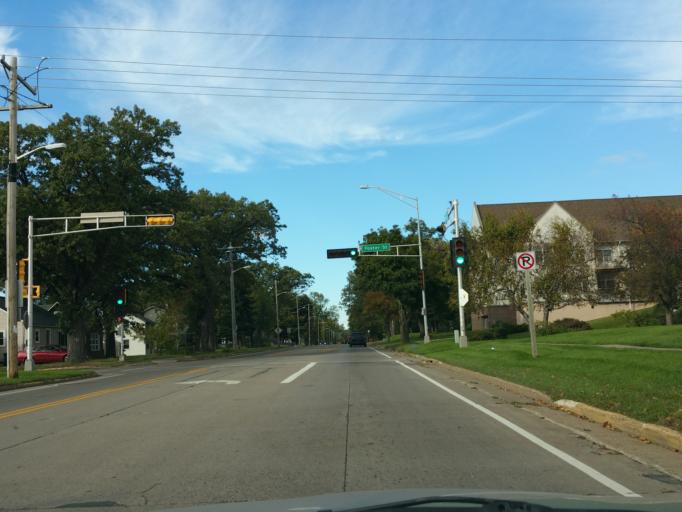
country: US
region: Wisconsin
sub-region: Pierce County
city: River Falls
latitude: 44.8476
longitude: -92.6293
